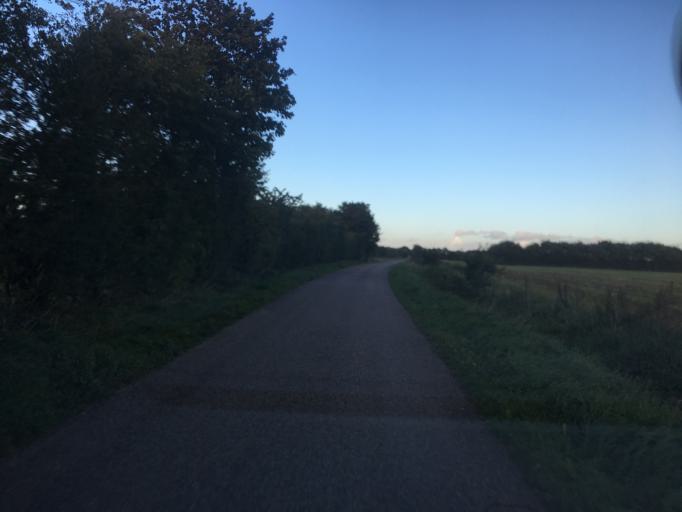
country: DE
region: Schleswig-Holstein
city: Ellhoft
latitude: 54.9618
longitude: 8.9921
